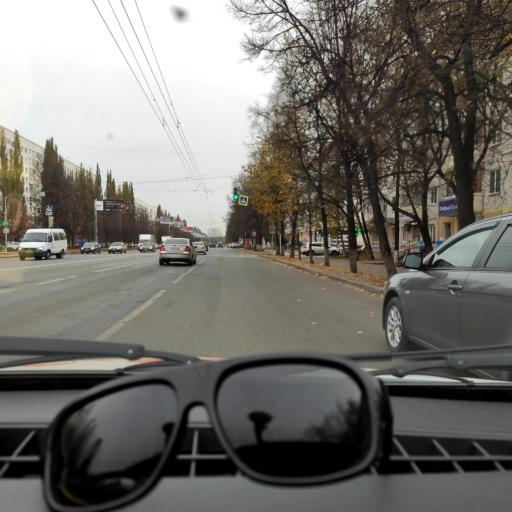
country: RU
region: Bashkortostan
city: Ufa
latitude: 54.7542
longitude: 55.9914
